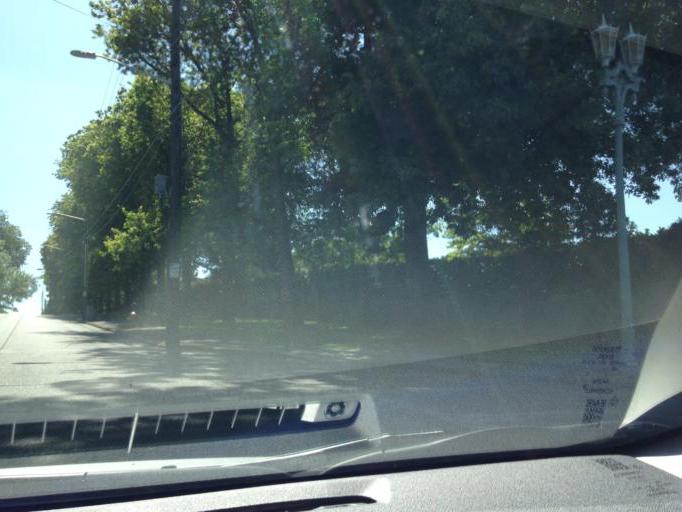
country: US
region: Washington
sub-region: King County
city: Seattle
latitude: 47.6301
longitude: -122.2865
